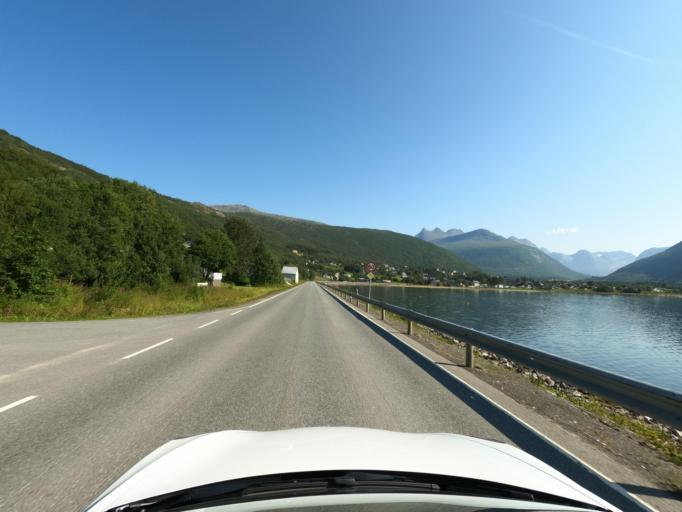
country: NO
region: Nordland
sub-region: Narvik
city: Bjerkvik
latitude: 68.3819
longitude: 17.5896
